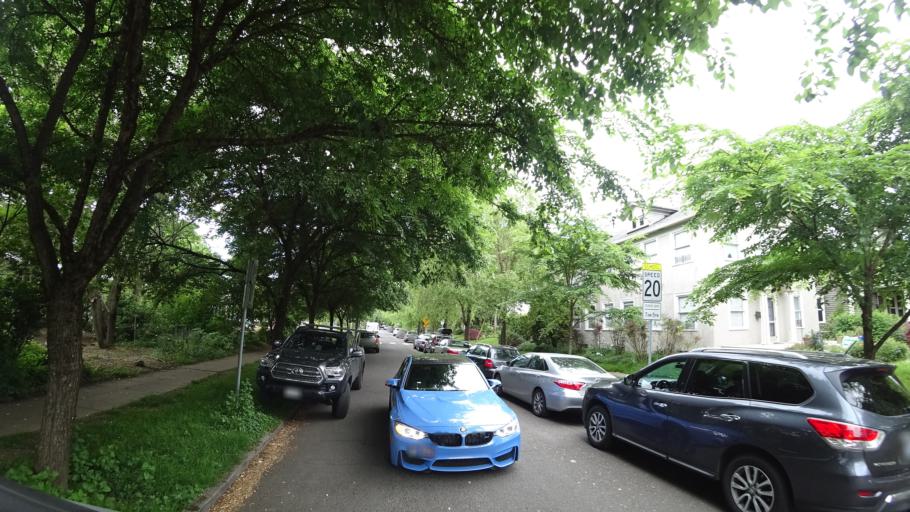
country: US
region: Oregon
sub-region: Multnomah County
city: Portland
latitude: 45.5063
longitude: -122.6505
